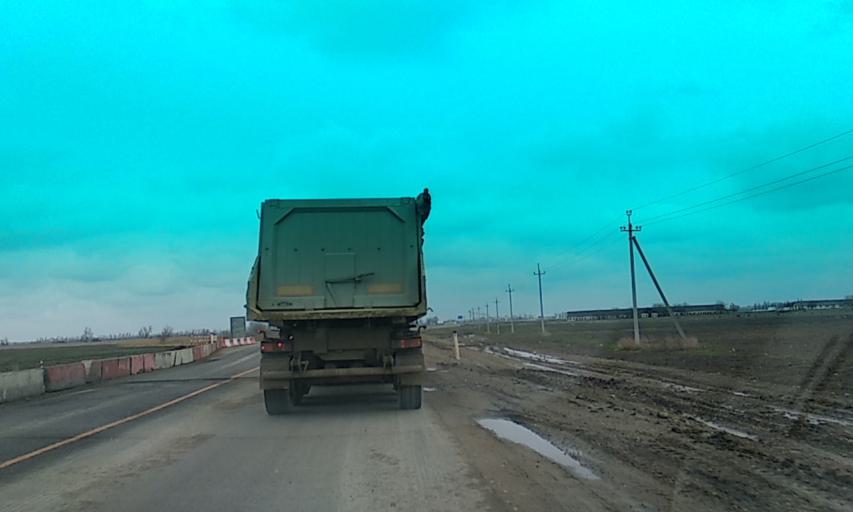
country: RU
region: Krasnodarskiy
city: Velikovechnoye
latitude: 44.9909
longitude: 39.7148
